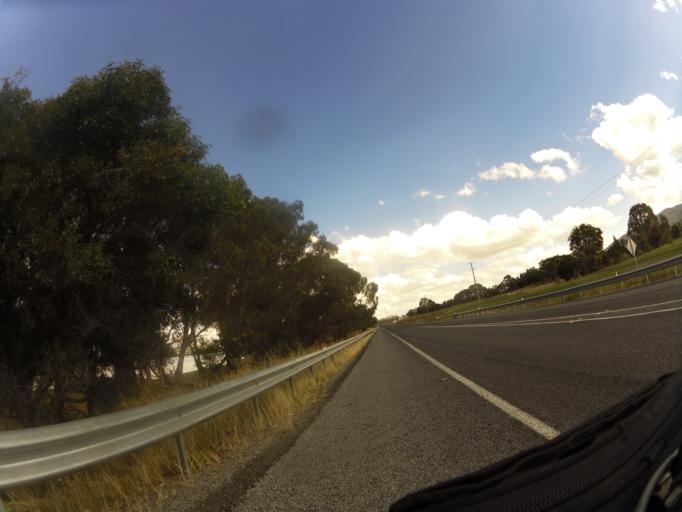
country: AU
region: Victoria
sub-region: Mansfield
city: Mansfield
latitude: -36.9005
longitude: 145.9970
